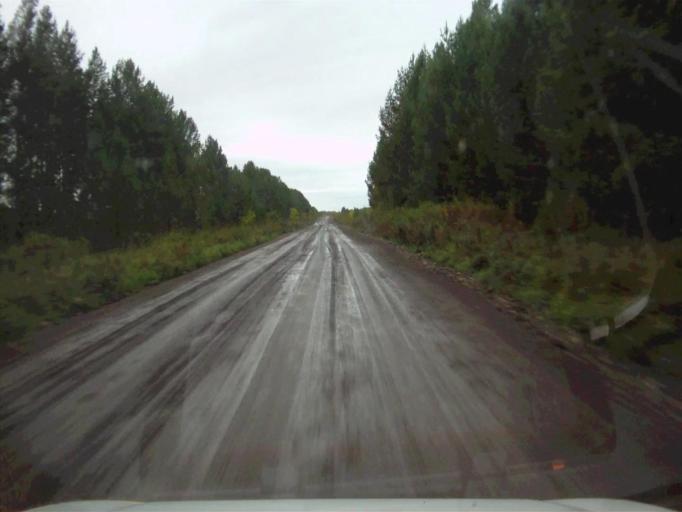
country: RU
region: Chelyabinsk
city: Nyazepetrovsk
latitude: 56.1429
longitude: 59.2882
